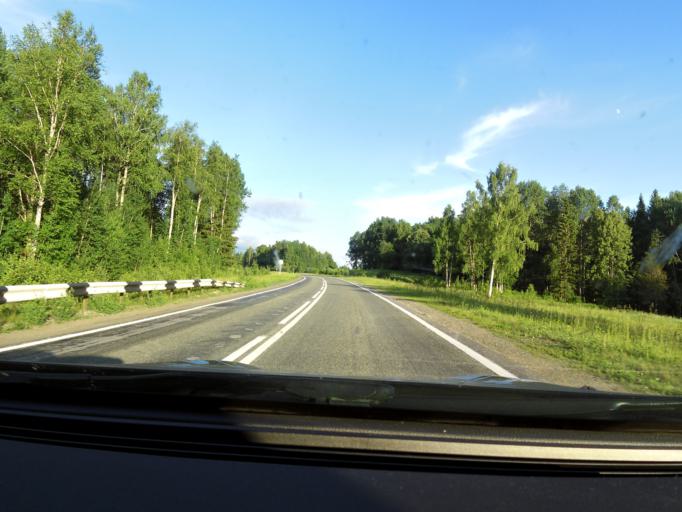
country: RU
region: Kirov
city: Kostino
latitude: 58.6432
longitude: 53.7993
